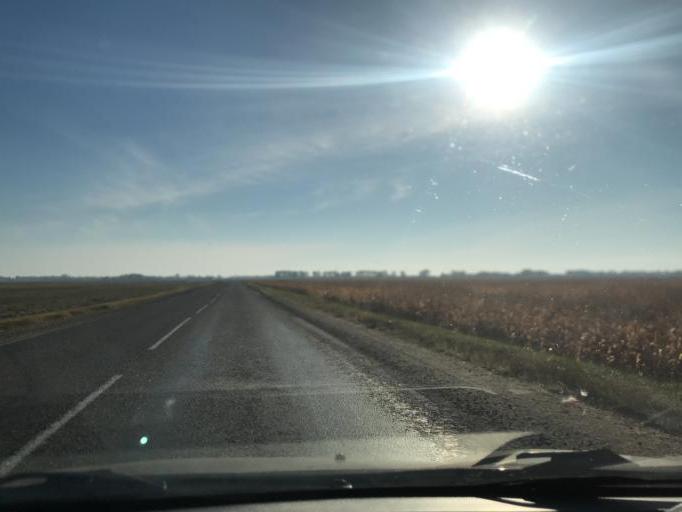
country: BY
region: Gomel
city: Brahin
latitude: 51.7817
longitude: 30.2233
